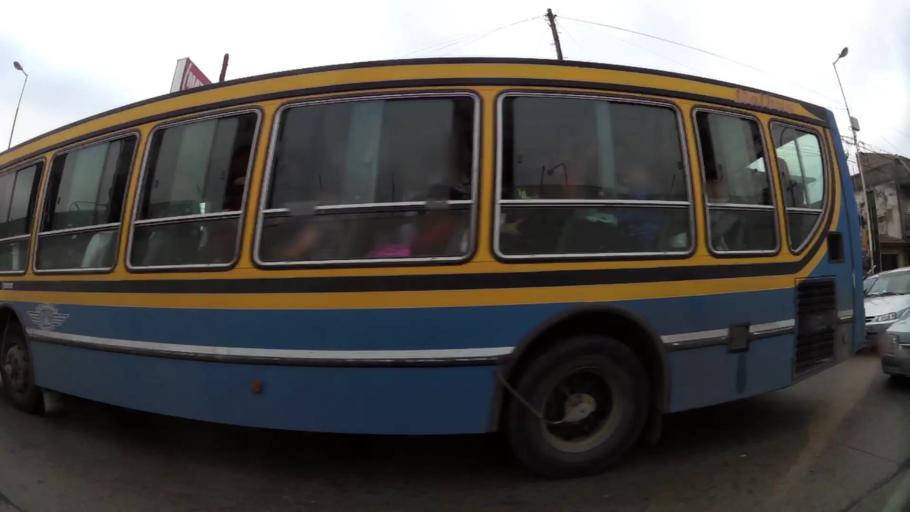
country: AR
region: Buenos Aires
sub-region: Partido de Moron
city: Moron
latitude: -34.6635
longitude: -58.5977
